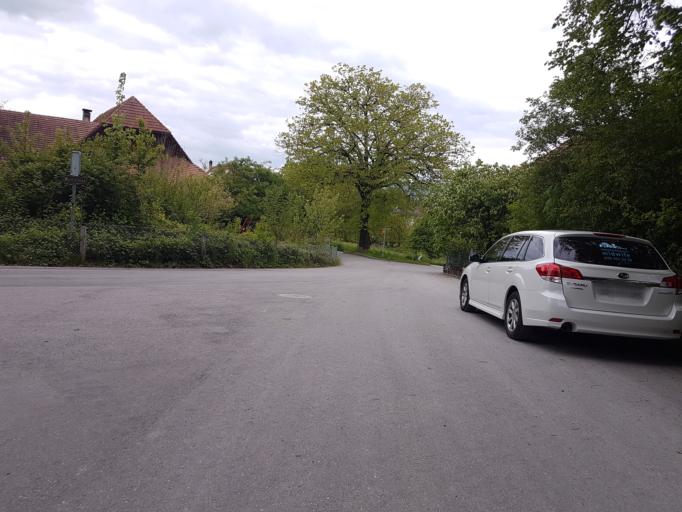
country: CH
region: Solothurn
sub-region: Bezirk Lebern
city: Langendorf
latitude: 47.1891
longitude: 7.5044
